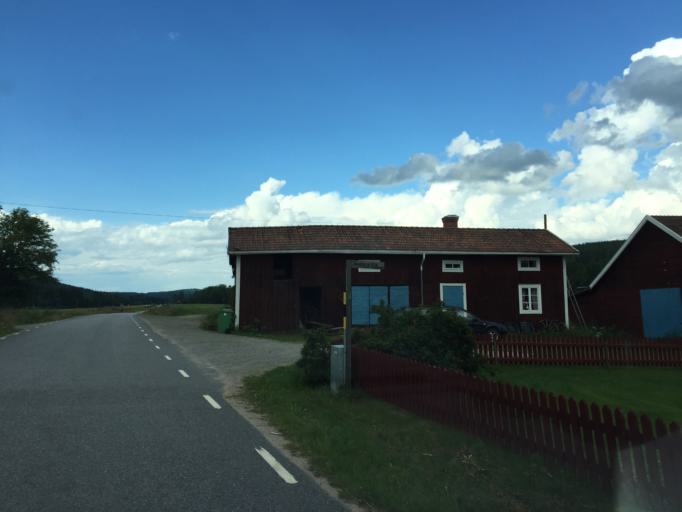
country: SE
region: Gaevleborg
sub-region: Ljusdals Kommun
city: Jaervsoe
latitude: 61.7148
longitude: 16.2956
